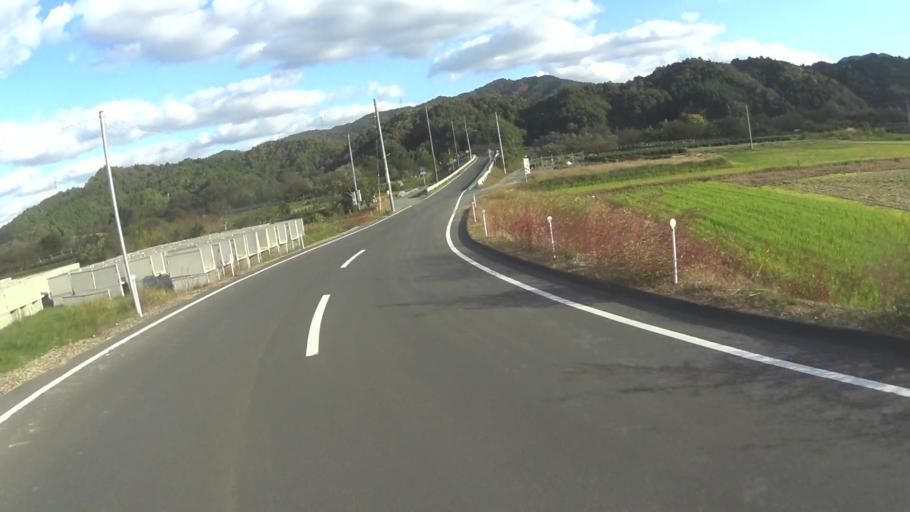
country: JP
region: Kyoto
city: Maizuru
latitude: 35.4298
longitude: 135.2523
